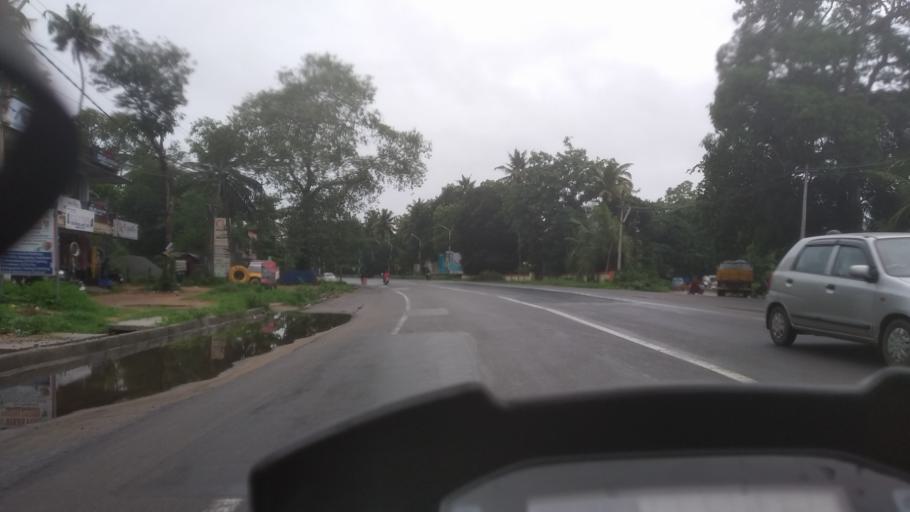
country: IN
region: Kerala
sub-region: Alappuzha
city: Kayankulam
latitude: 9.1512
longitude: 76.5130
